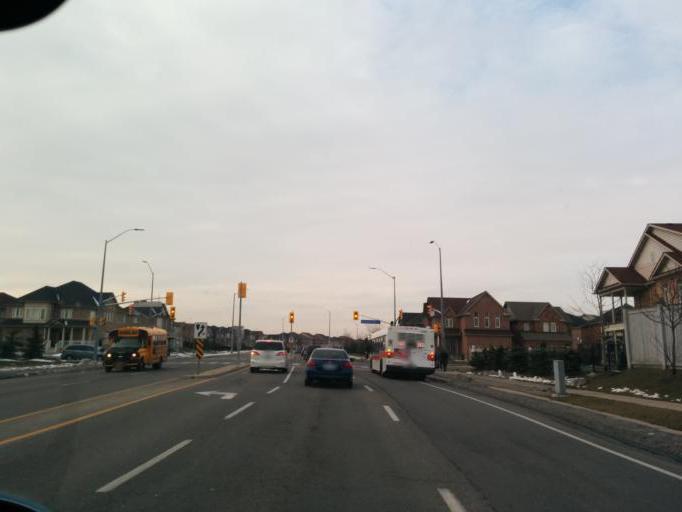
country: CA
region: Ontario
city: Mississauga
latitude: 43.5942
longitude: -79.6579
